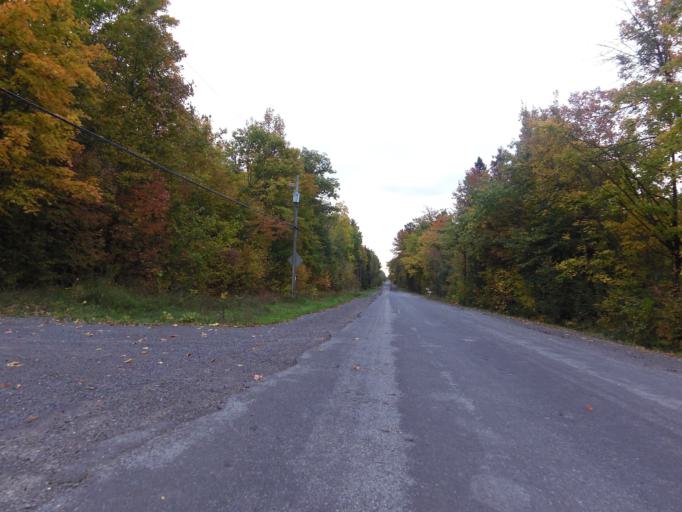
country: CA
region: Ontario
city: Arnprior
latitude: 45.4783
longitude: -76.1639
